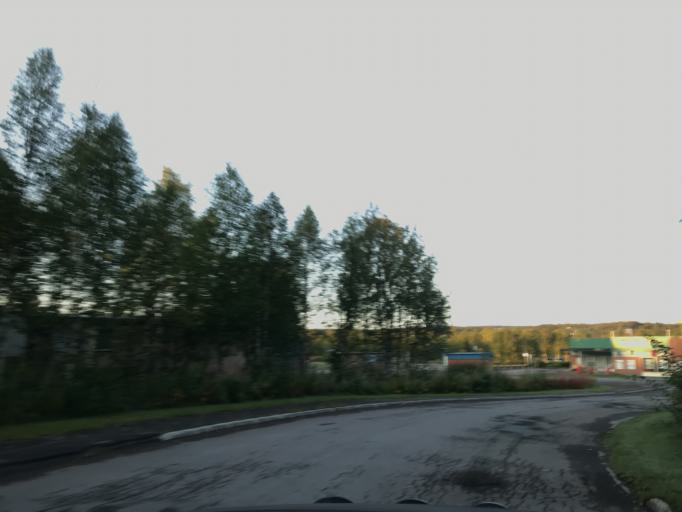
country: SE
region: Norrbotten
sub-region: Gallivare Kommun
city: Malmberget
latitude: 67.6494
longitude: 21.0501
